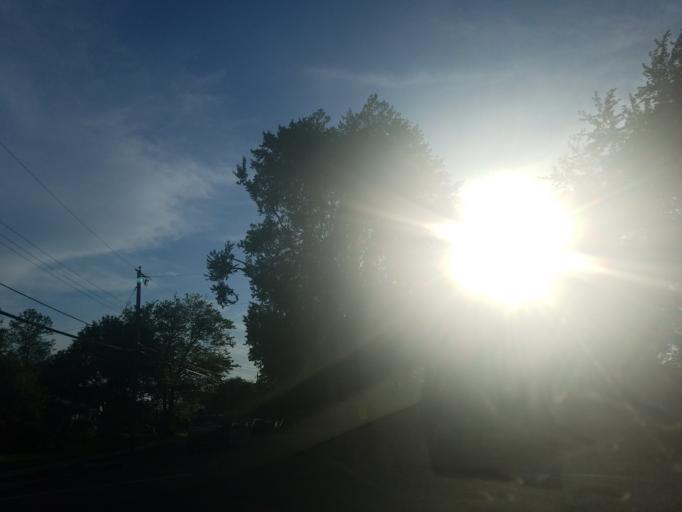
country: US
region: Virginia
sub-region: Fairfax County
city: Vienna
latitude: 38.8885
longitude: -77.2649
